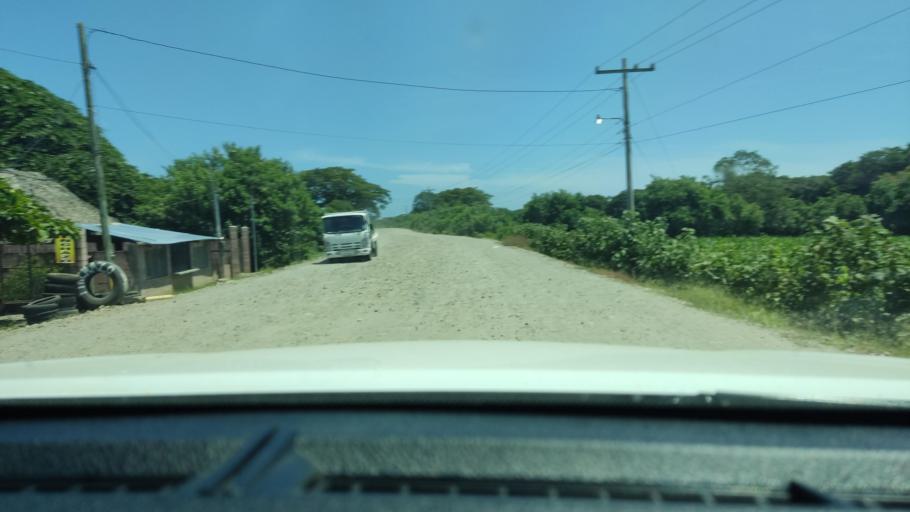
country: SV
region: Ahuachapan
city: San Francisco Menendez
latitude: 13.7882
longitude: -90.1185
